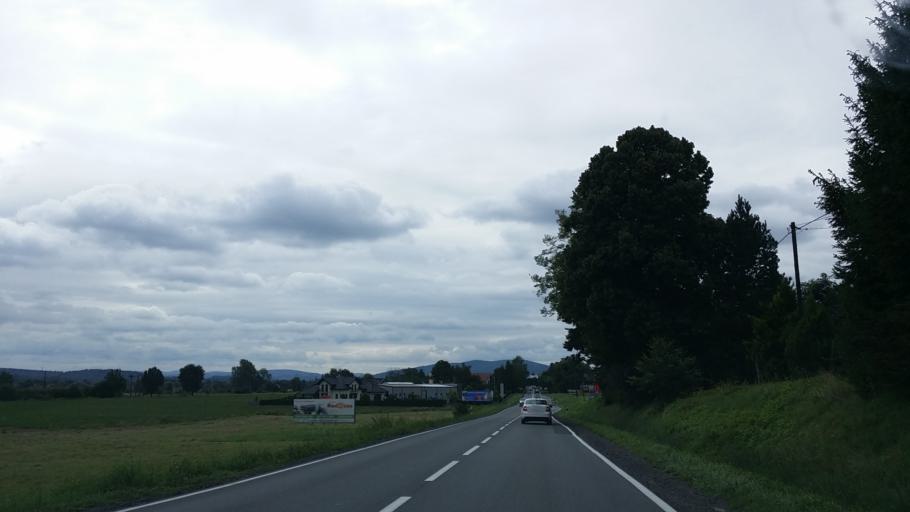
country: PL
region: Lesser Poland Voivodeship
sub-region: Powiat wadowicki
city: Radocza
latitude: 49.9204
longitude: 19.4799
